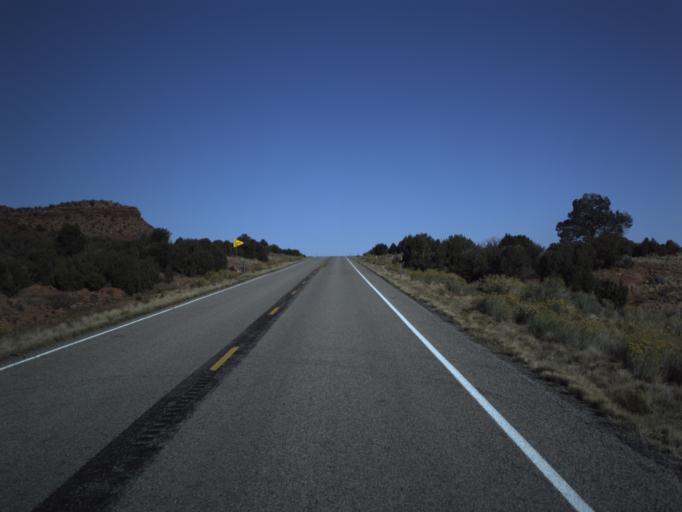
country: US
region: Utah
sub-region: San Juan County
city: Blanding
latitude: 37.6446
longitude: -110.1656
